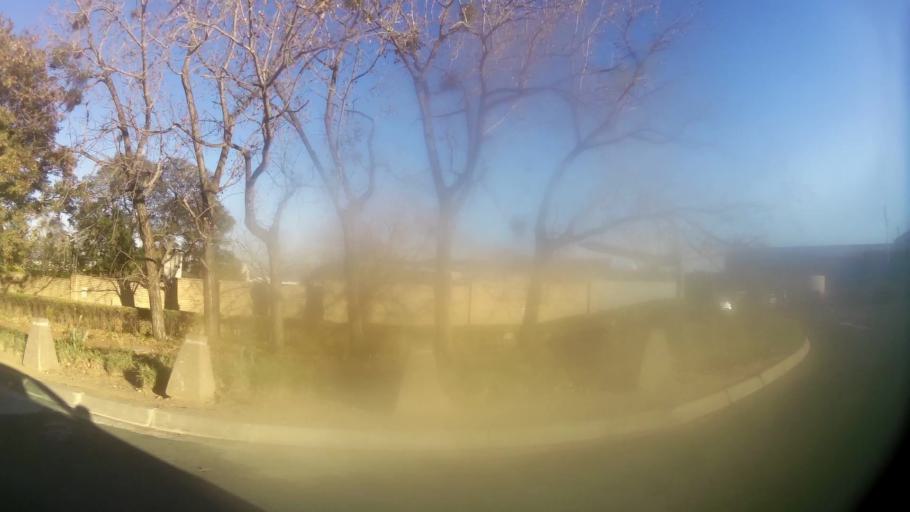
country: ZA
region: Gauteng
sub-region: City of Johannesburg Metropolitan Municipality
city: Midrand
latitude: -26.0115
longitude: 28.1202
